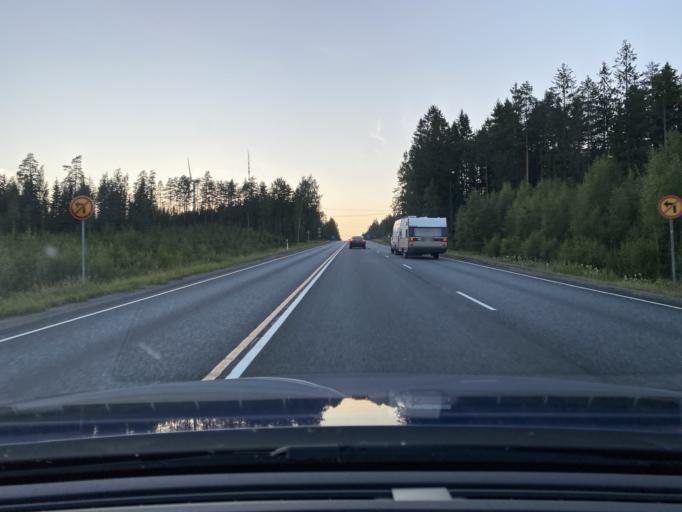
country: FI
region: Pirkanmaa
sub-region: Luoteis-Pirkanmaa
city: Ikaalinen
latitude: 61.7790
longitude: 23.0033
